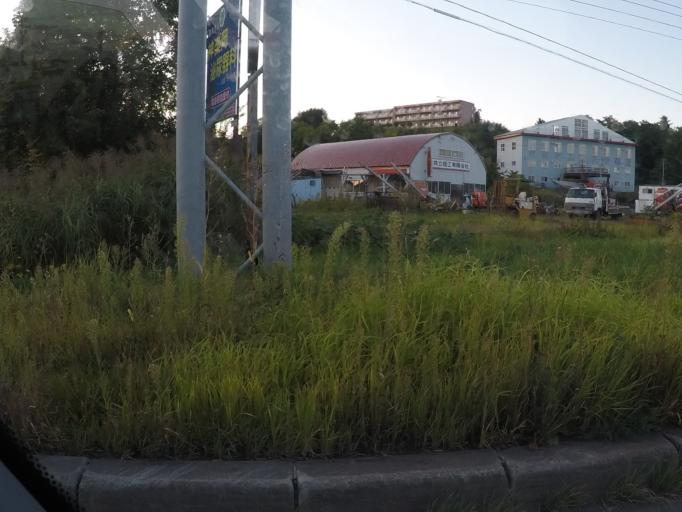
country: JP
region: Hokkaido
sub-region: Asahikawa-shi
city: Asahikawa
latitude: 43.5976
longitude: 142.4637
